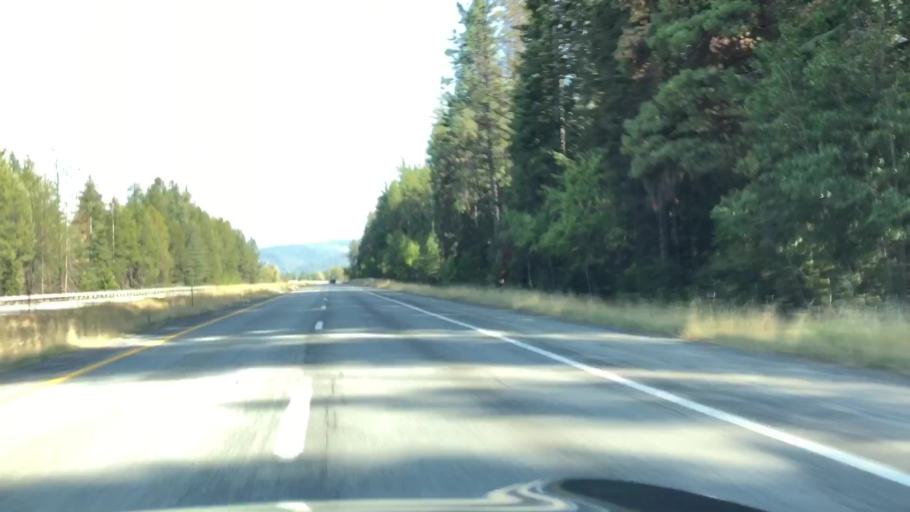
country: US
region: Idaho
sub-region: Shoshone County
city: Pinehurst
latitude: 47.5626
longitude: -116.4011
